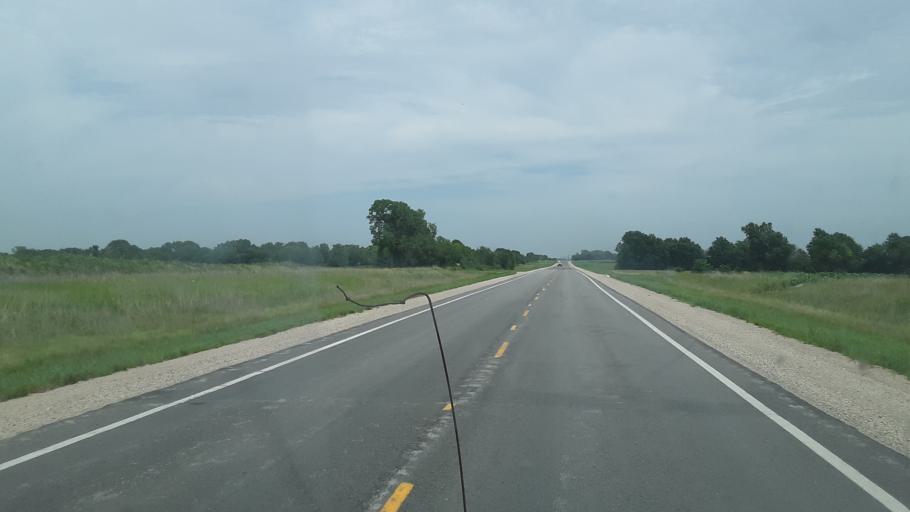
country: US
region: Kansas
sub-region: Woodson County
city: Yates Center
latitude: 37.9117
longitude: -95.5859
